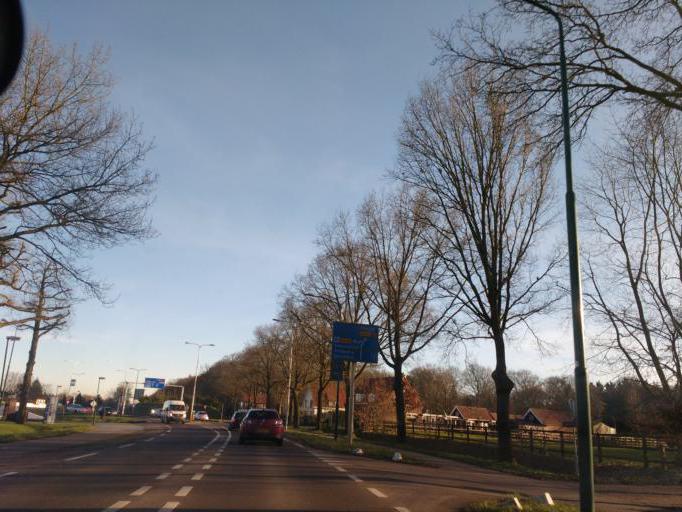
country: NL
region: Utrecht
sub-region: Gemeente Veenendaal
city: Veenendaal
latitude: 51.9986
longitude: 5.5500
